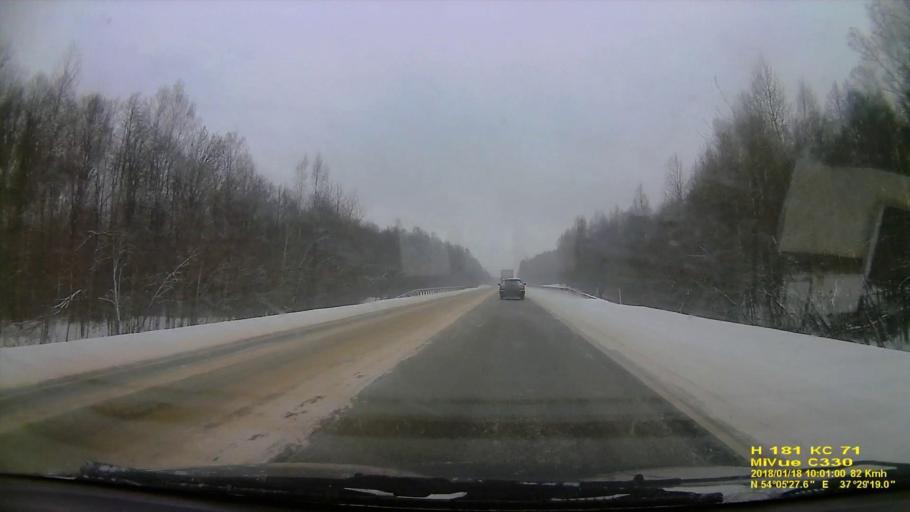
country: RU
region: Tula
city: Pervomayskiy
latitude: 54.0910
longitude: 37.4886
